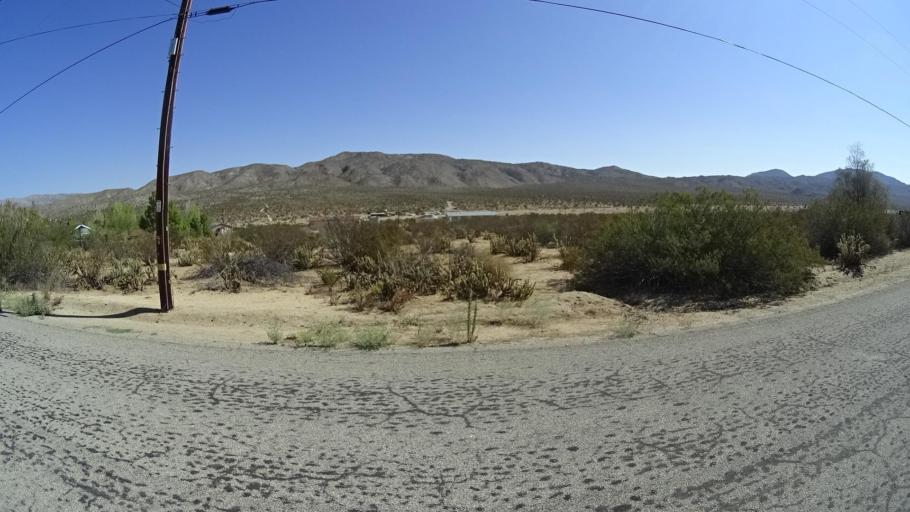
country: US
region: California
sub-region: San Diego County
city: Julian
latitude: 33.0722
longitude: -116.4361
